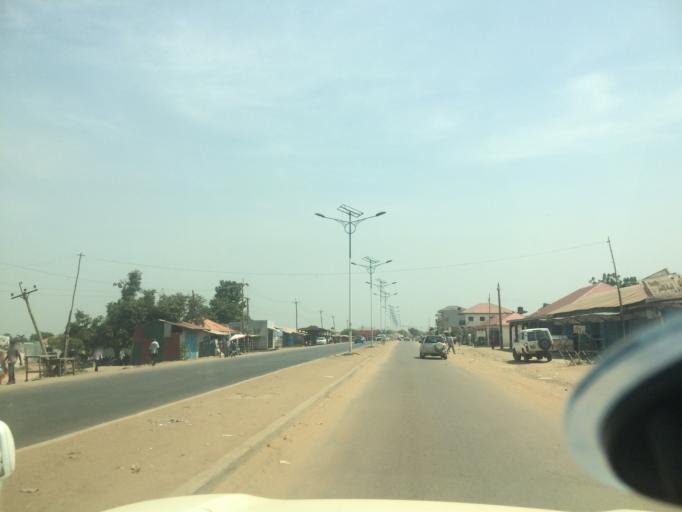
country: SS
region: Central Equatoria
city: Juba
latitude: 4.8646
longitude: 31.5589
